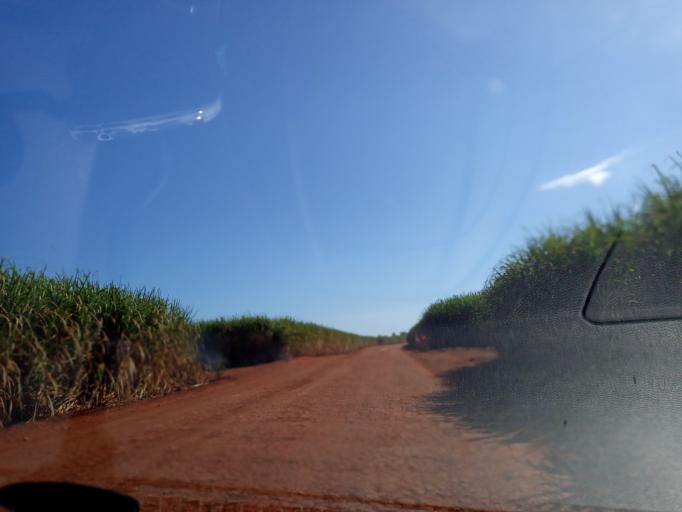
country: BR
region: Goias
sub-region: Itumbiara
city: Itumbiara
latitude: -18.4484
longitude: -49.1781
